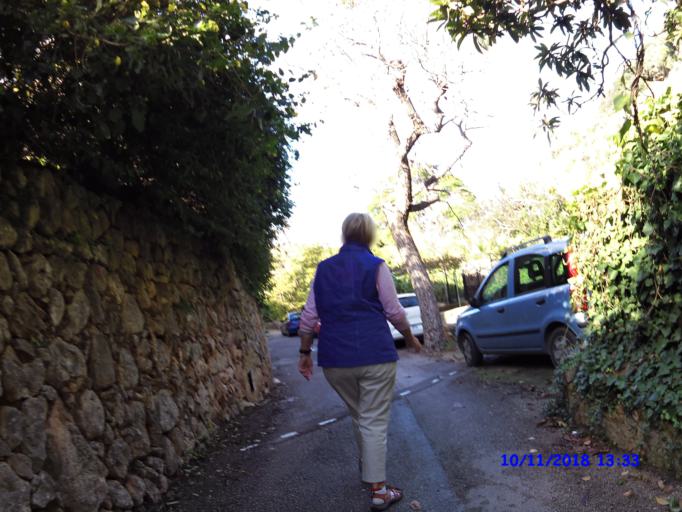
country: ES
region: Balearic Islands
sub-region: Illes Balears
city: Deia
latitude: 39.7467
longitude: 2.6455
